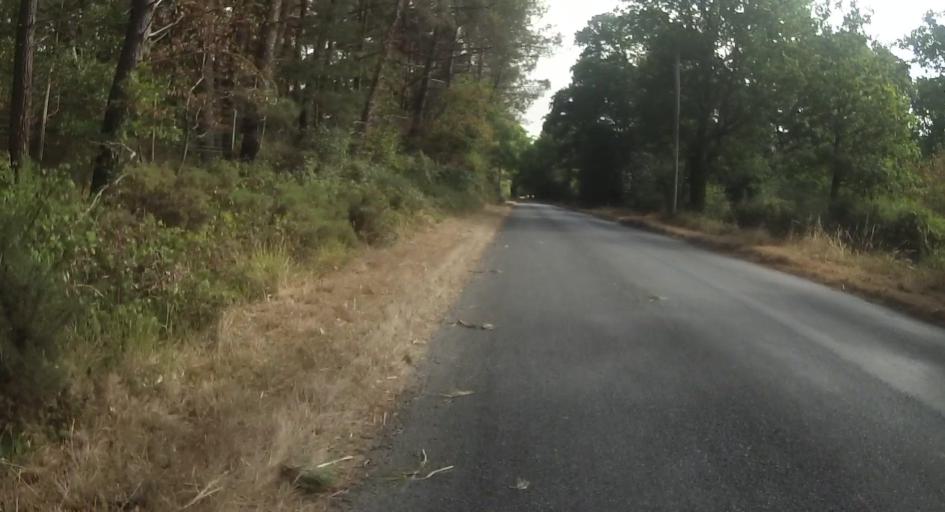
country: GB
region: England
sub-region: Dorset
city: Wareham
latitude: 50.6664
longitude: -2.1146
